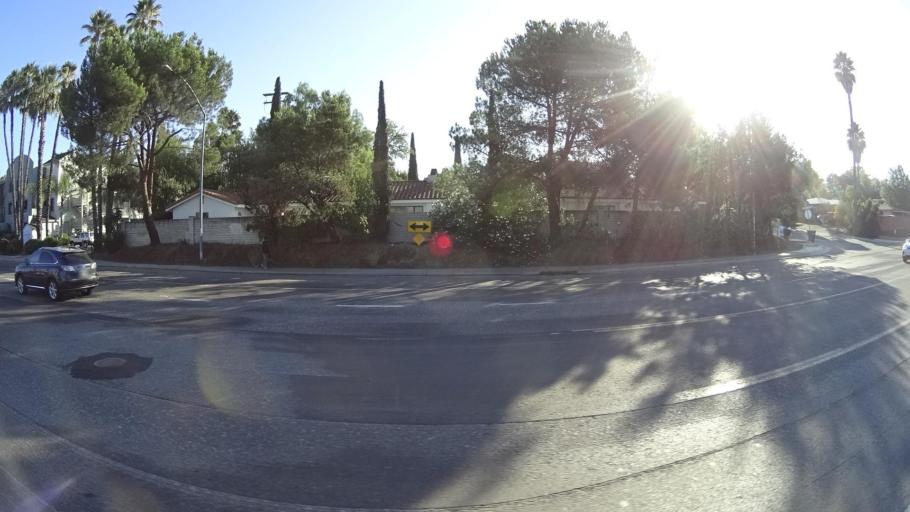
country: US
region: California
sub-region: San Diego County
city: Escondido
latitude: 33.1263
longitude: -117.0651
